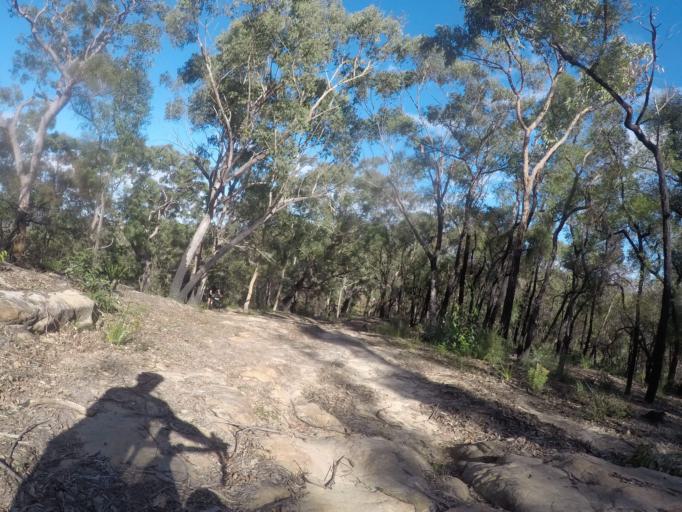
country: AU
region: New South Wales
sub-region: Hornsby Shire
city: Glenorie
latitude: -33.3424
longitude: 151.0583
